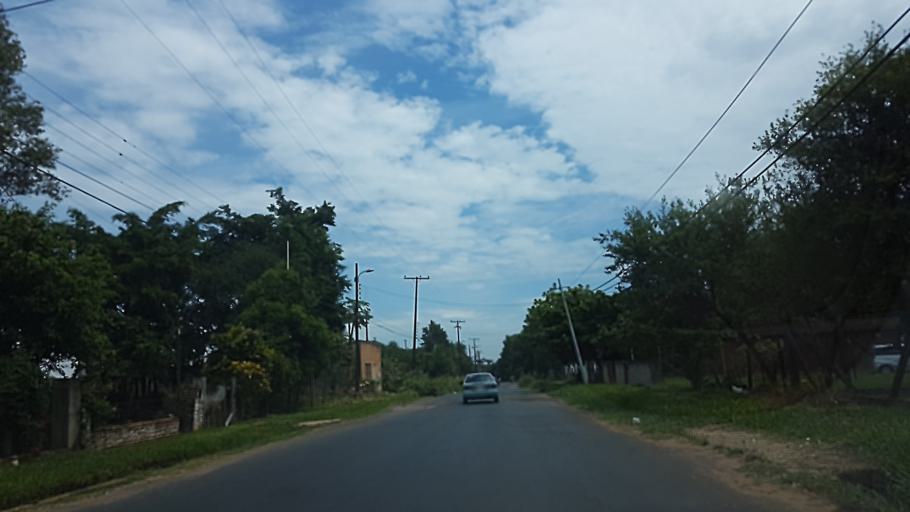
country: PY
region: Central
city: San Lorenzo
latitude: -25.2819
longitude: -57.4955
